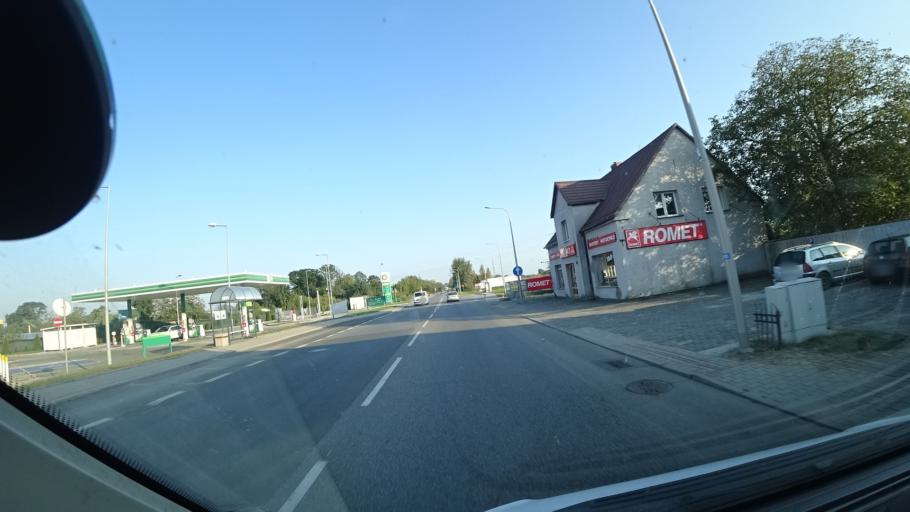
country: PL
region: Opole Voivodeship
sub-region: Powiat kedzierzynsko-kozielski
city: Kozle
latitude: 50.3404
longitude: 18.1760
